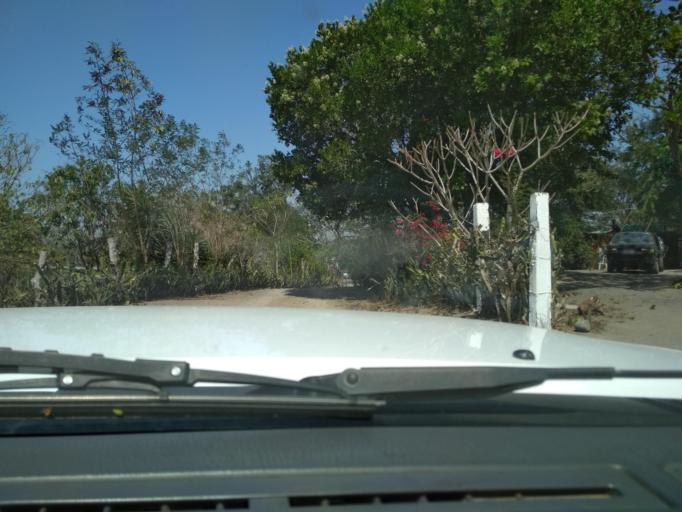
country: MX
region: Veracruz
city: Manlio Fabio Altamirano
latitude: 19.1555
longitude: -96.3282
